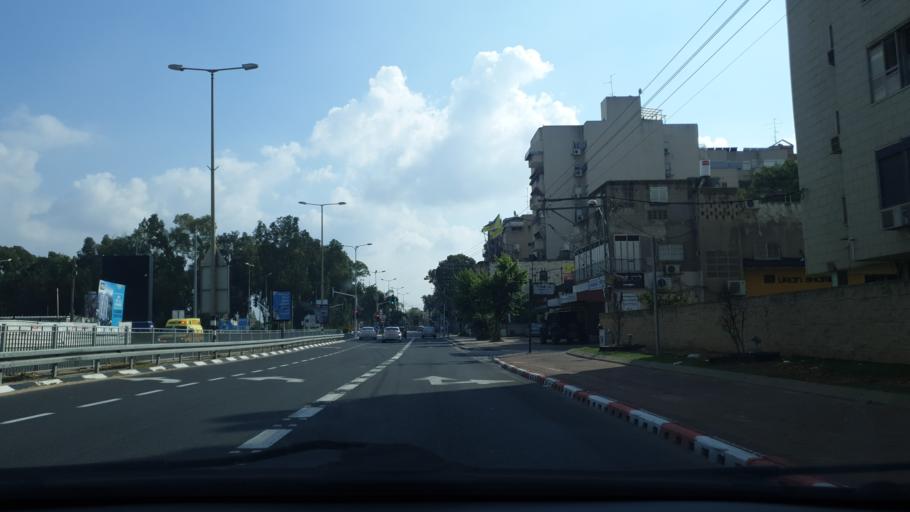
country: IL
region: Central District
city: Ramla
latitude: 31.9391
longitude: 34.8656
